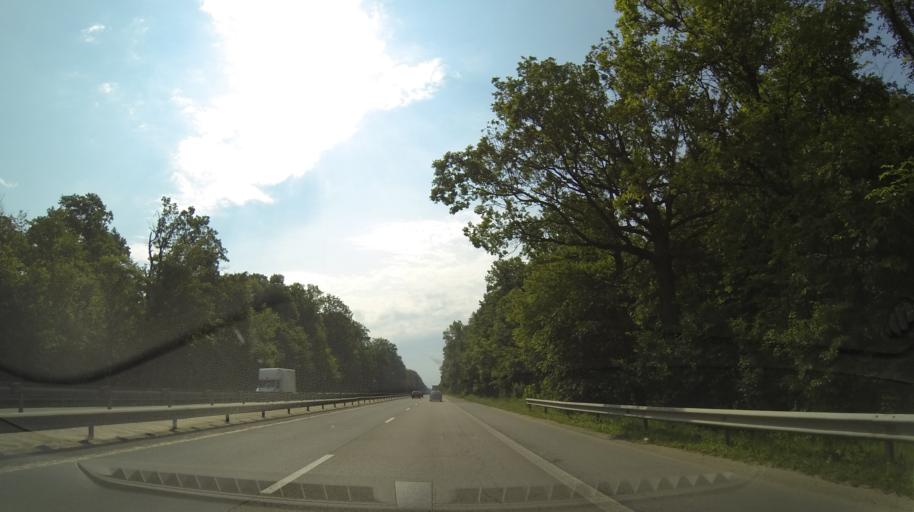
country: RO
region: Giurgiu
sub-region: Comuna Vanatorii Mici
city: Vanatorii Mici
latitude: 44.5124
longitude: 25.5645
